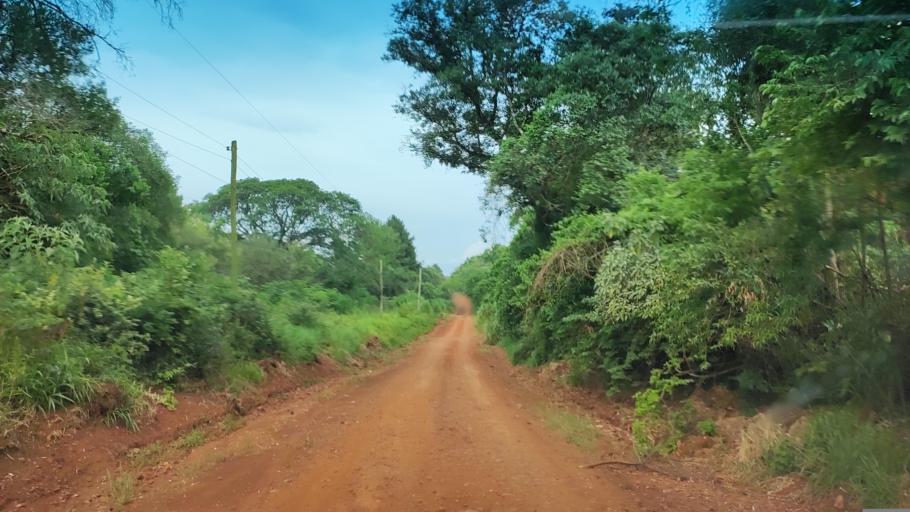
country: AR
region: Misiones
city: Gobernador Roca
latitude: -27.1488
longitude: -55.4806
